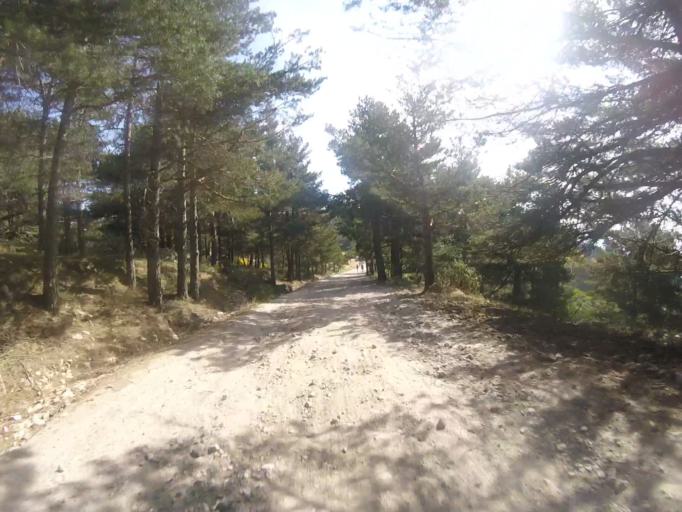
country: ES
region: Madrid
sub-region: Provincia de Madrid
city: Guadarrama
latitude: 40.6929
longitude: -4.1494
